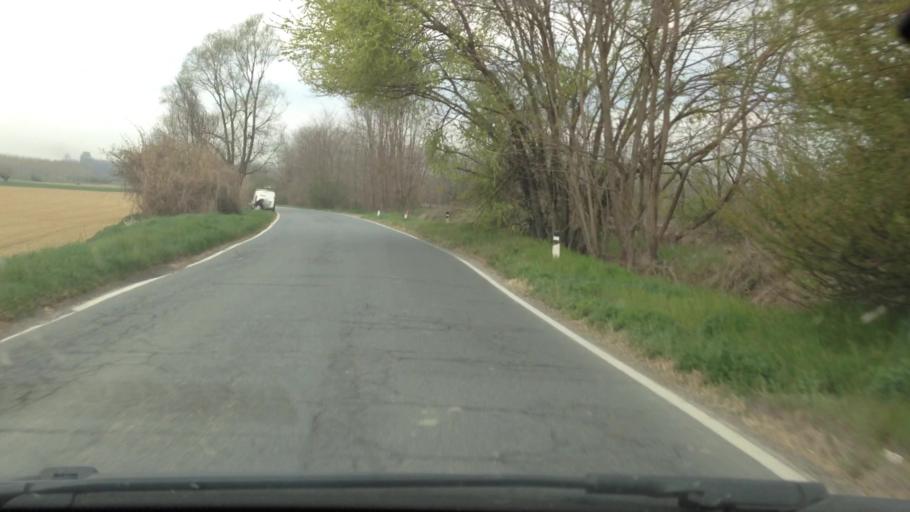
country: IT
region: Piedmont
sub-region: Provincia di Asti
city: Revigliasco d'Asti
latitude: 44.8959
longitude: 8.1679
